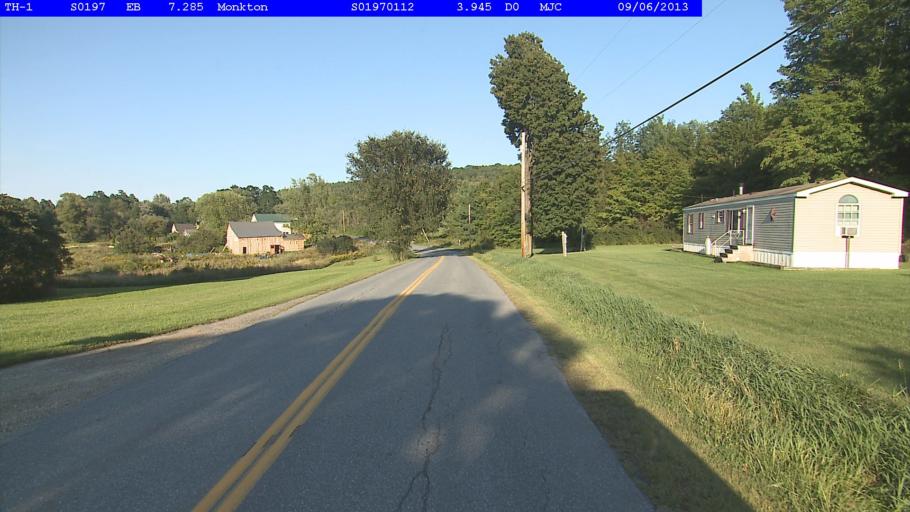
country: US
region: Vermont
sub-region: Chittenden County
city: Hinesburg
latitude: 44.2331
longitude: -73.1494
